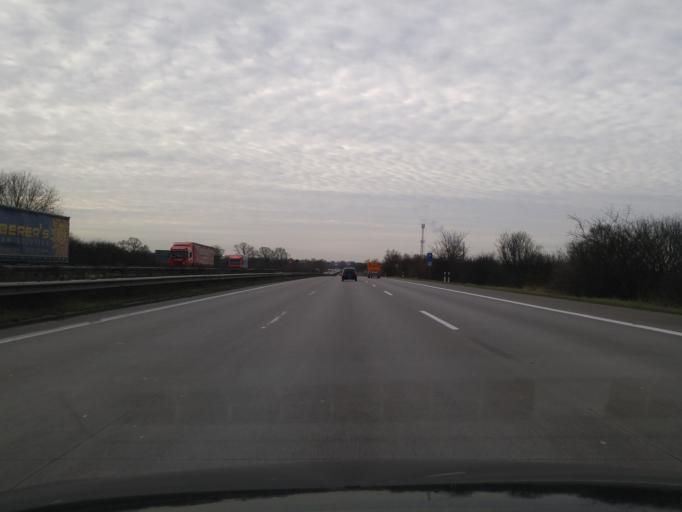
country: DE
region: Schleswig-Holstein
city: Braak
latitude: 53.6336
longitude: 10.2551
